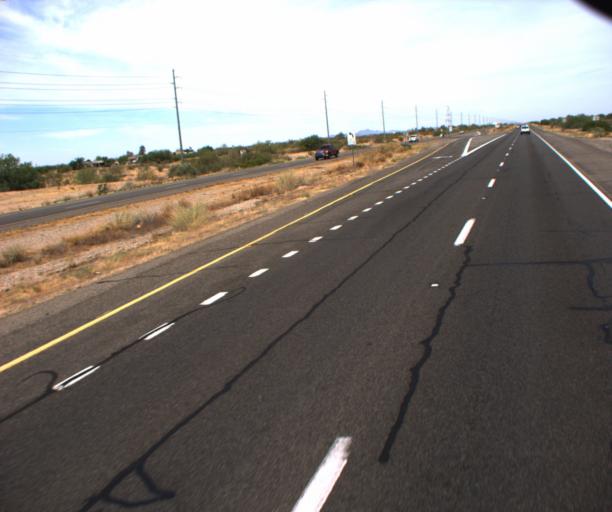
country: US
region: Arizona
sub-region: Maricopa County
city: Sun City West
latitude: 33.7253
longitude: -112.4610
